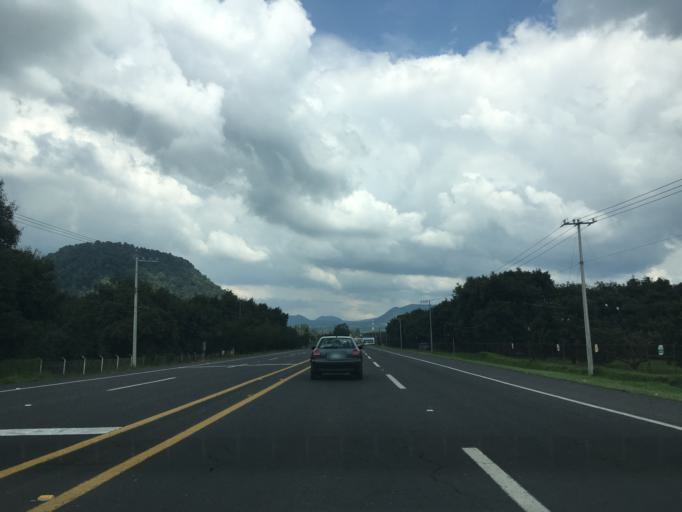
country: MX
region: Michoacan
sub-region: Uruapan
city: Uruapan
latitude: 19.4525
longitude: -102.0763
